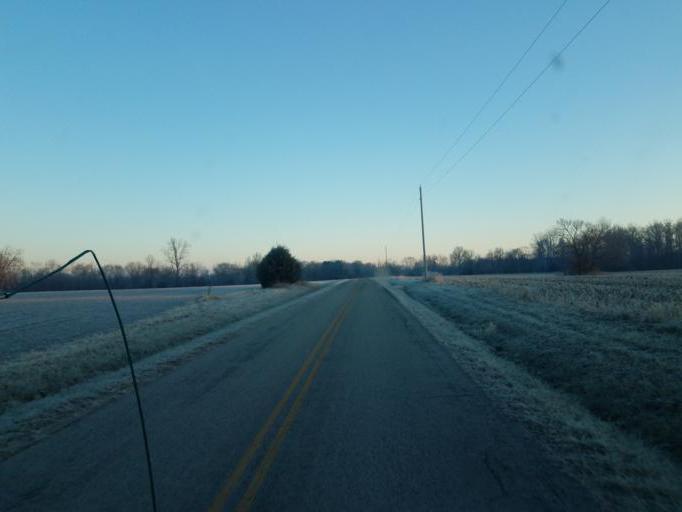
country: US
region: Ohio
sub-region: Delaware County
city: Ashley
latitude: 40.5180
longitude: -83.0189
